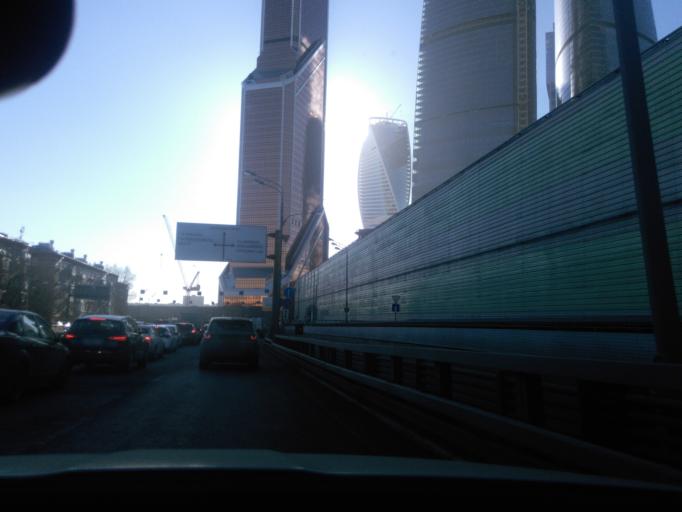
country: RU
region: Moskovskaya
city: Presnenskiy
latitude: 55.7523
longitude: 37.5345
